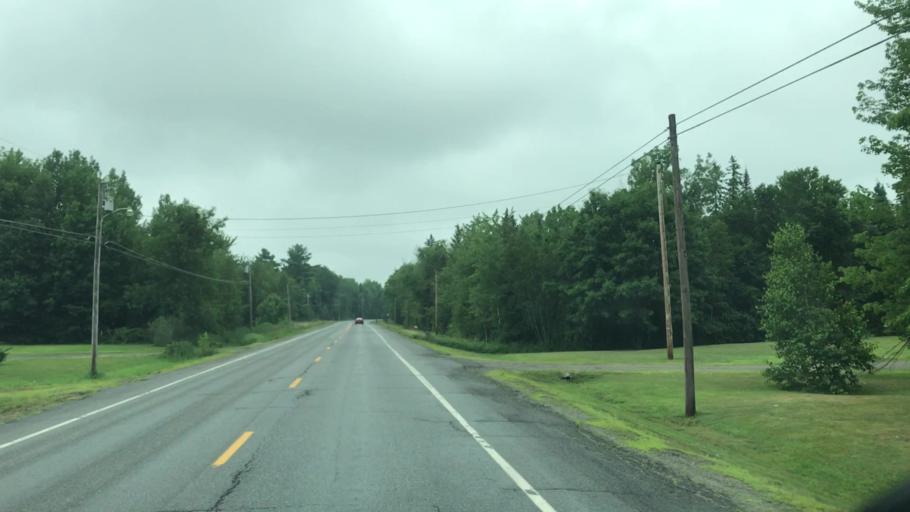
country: US
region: Maine
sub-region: Penobscot County
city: Howland
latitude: 45.2661
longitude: -68.6385
